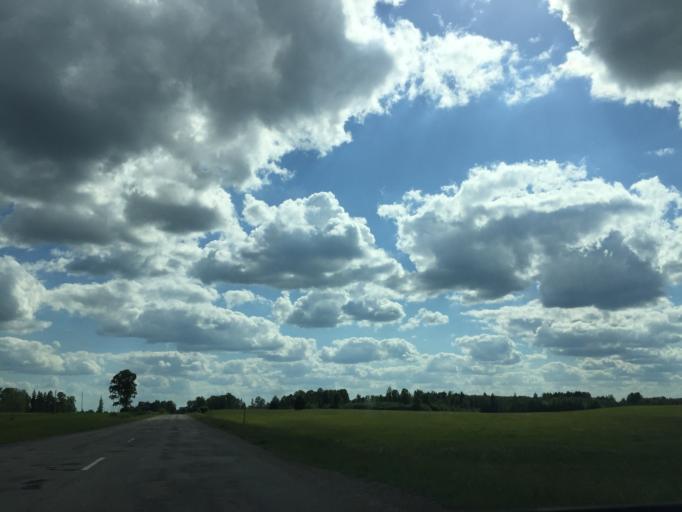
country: LV
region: Jaunpils
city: Jaunpils
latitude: 56.8586
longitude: 23.0530
